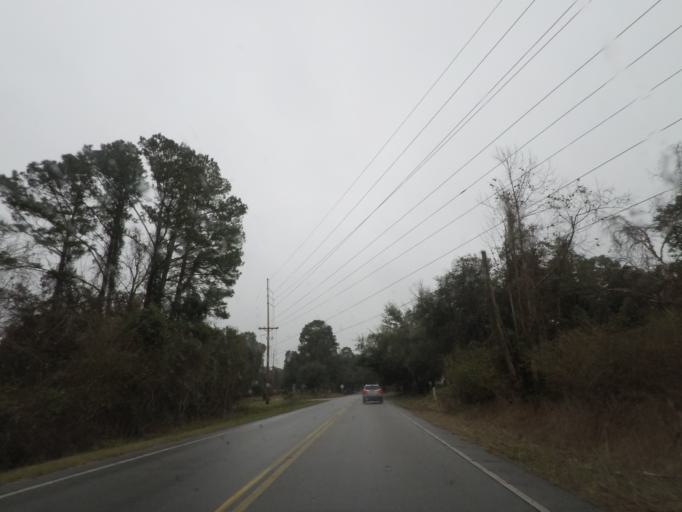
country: US
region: South Carolina
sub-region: Charleston County
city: Seabrook Island
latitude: 32.5707
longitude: -80.2834
